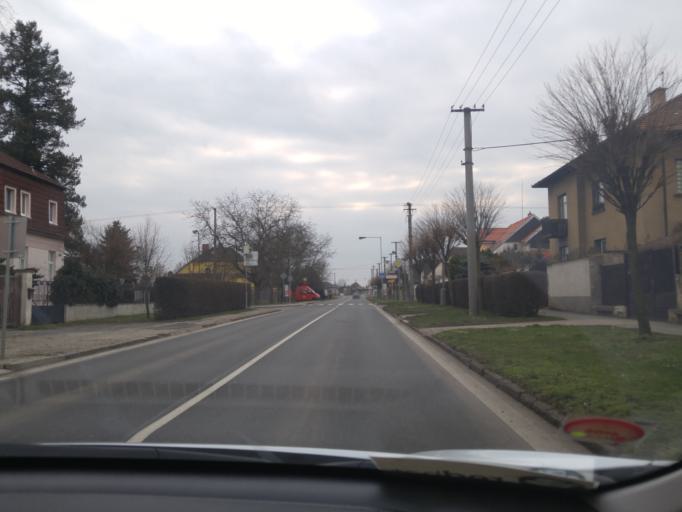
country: CZ
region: Central Bohemia
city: Tisice
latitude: 50.2365
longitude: 14.5503
